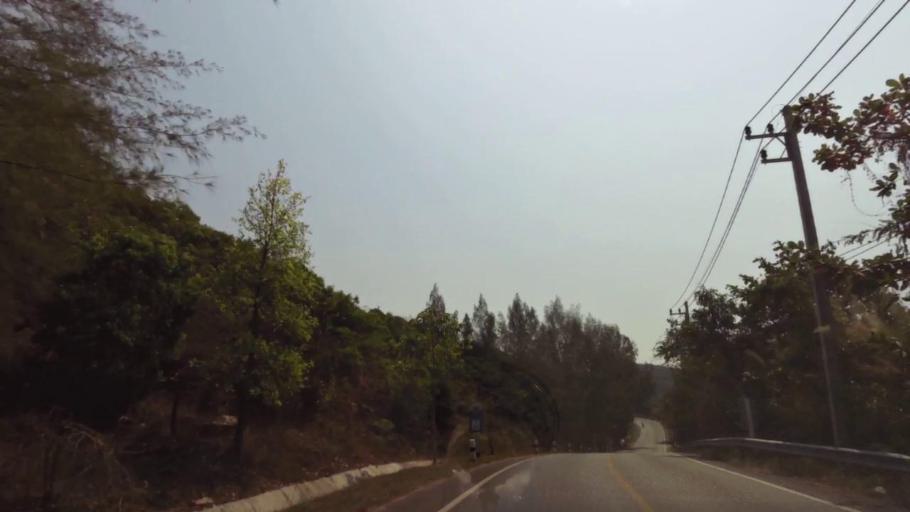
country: TH
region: Chanthaburi
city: Tha Mai
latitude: 12.5298
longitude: 101.9460
